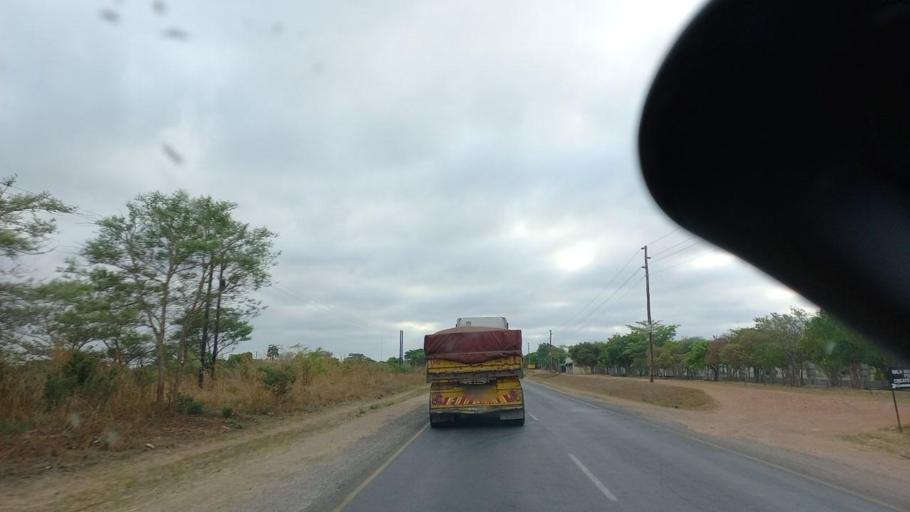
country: ZM
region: Lusaka
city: Chongwe
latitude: -15.3517
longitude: 28.5557
